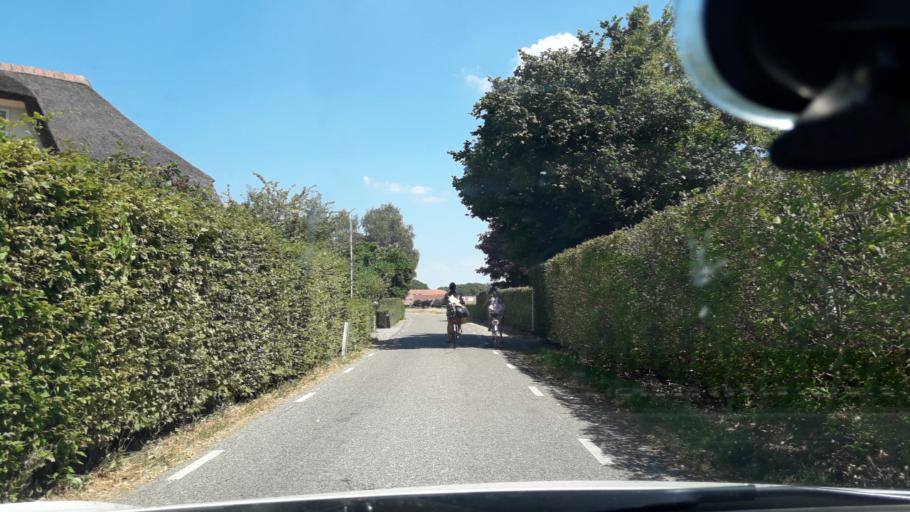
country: NL
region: Gelderland
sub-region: Gemeente Brummen
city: Brummen
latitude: 52.0984
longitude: 6.1767
